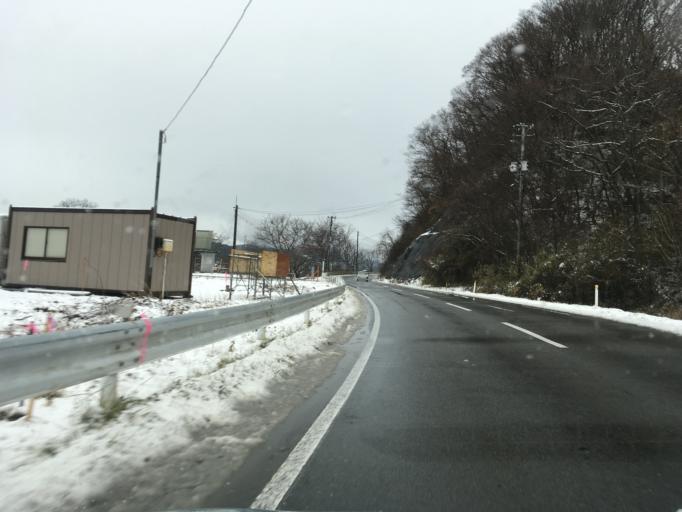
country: JP
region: Iwate
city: Ichinoseki
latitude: 38.8899
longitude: 141.2664
